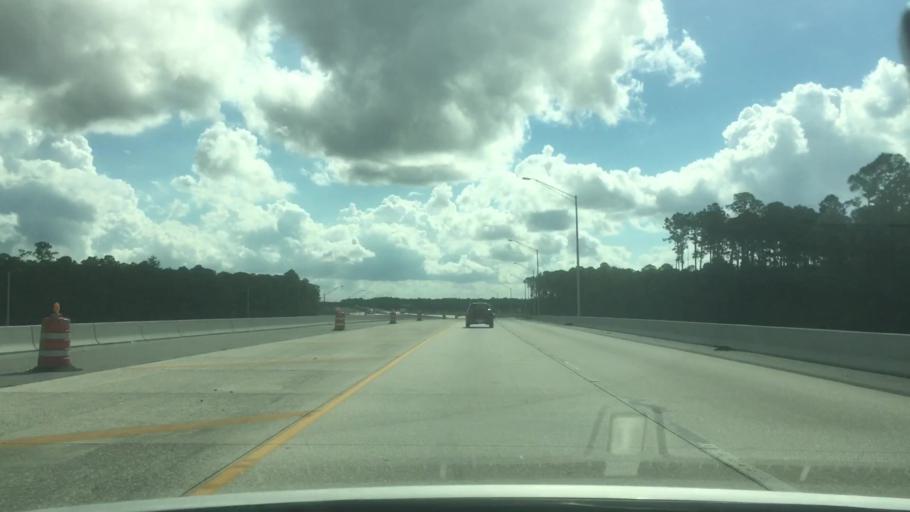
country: US
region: Florida
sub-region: Saint Johns County
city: Palm Valley
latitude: 30.1774
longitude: -81.5139
